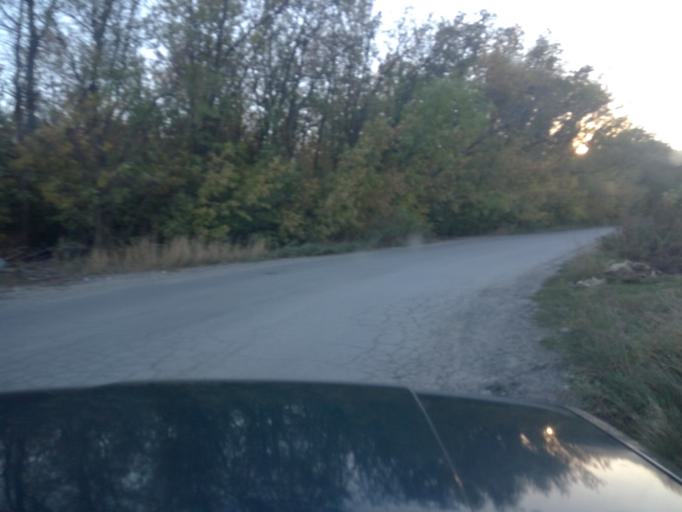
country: RU
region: Rostov
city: Temernik
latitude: 47.3556
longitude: 39.7402
